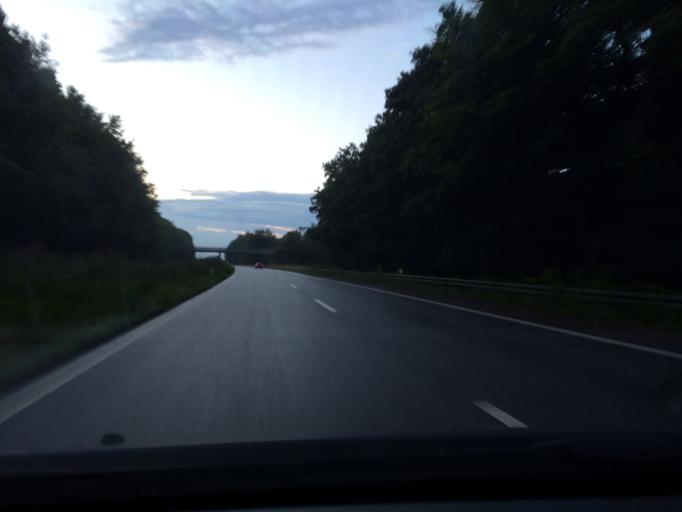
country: DK
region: Zealand
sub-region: Koge Kommune
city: Ejby
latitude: 55.4509
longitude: 12.1225
